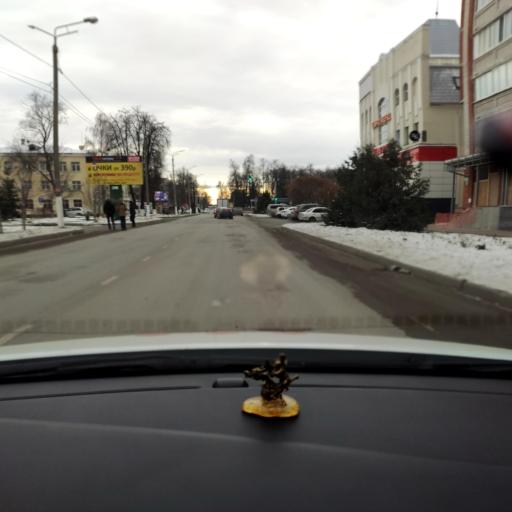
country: RU
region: Tatarstan
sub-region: Zelenodol'skiy Rayon
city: Zelenodolsk
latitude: 55.8480
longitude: 48.5013
